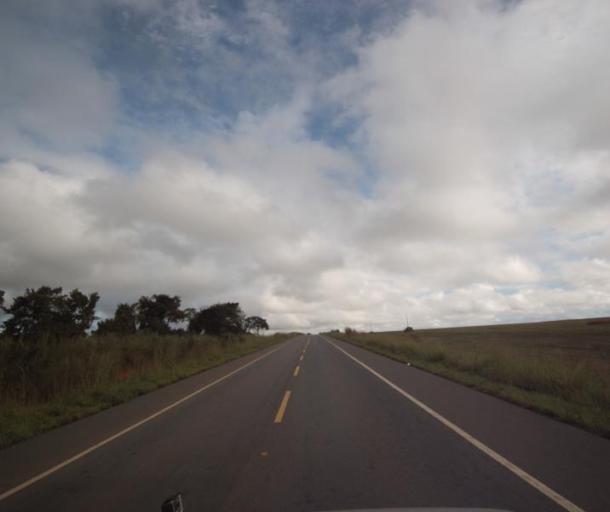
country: BR
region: Goias
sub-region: Barro Alto
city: Barro Alto
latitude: -15.2982
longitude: -48.6733
